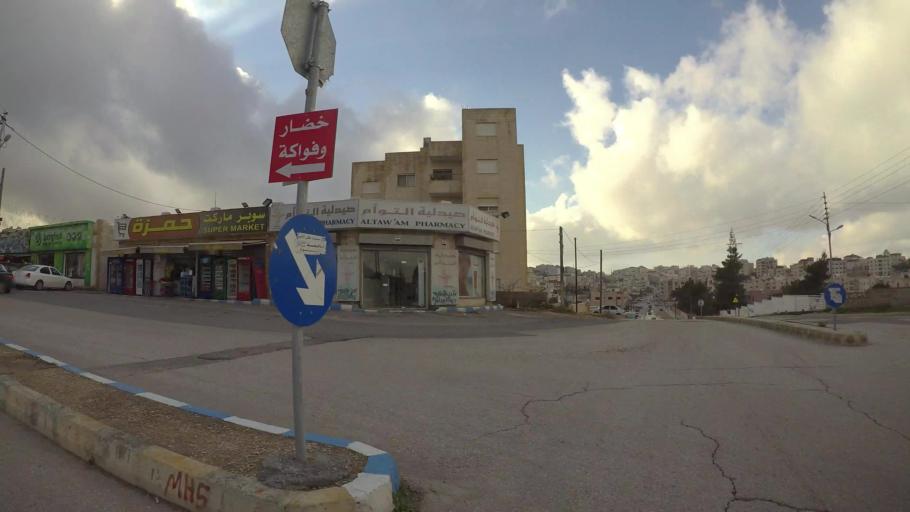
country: JO
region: Amman
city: Al Jubayhah
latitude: 32.0490
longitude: 35.9037
